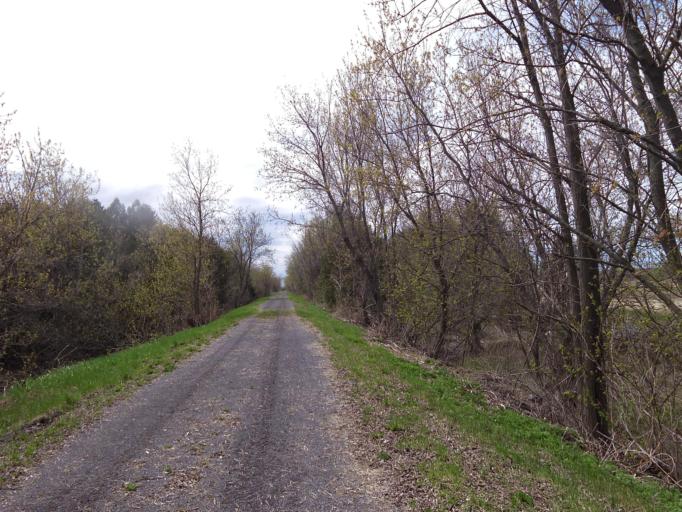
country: CA
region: Ontario
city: Hawkesbury
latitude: 45.5423
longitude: -74.7567
